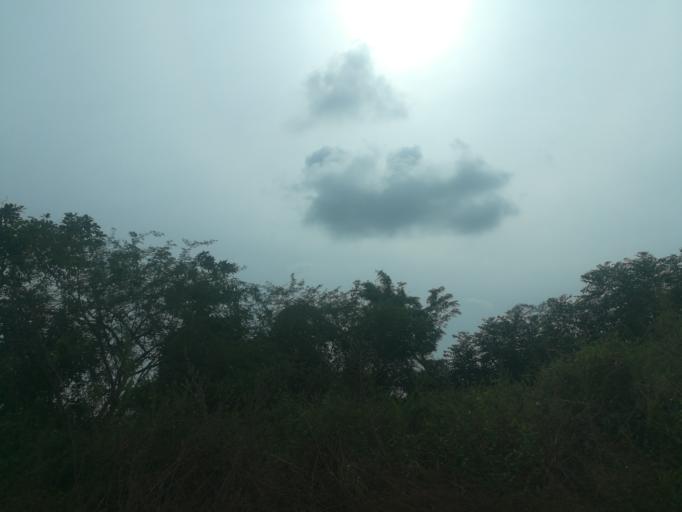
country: NG
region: Ogun
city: Ayetoro
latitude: 7.2917
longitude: 3.0796
